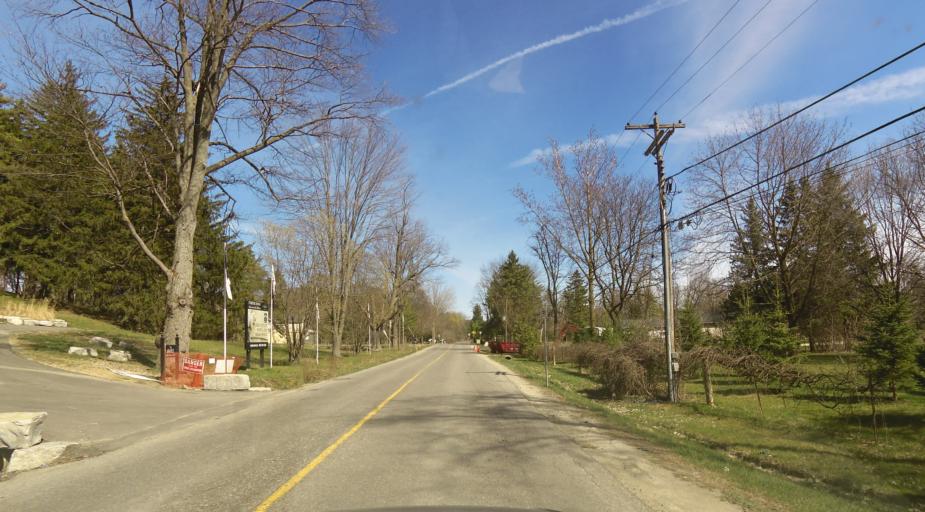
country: CA
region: Ontario
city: Brampton
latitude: 43.6472
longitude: -79.7775
